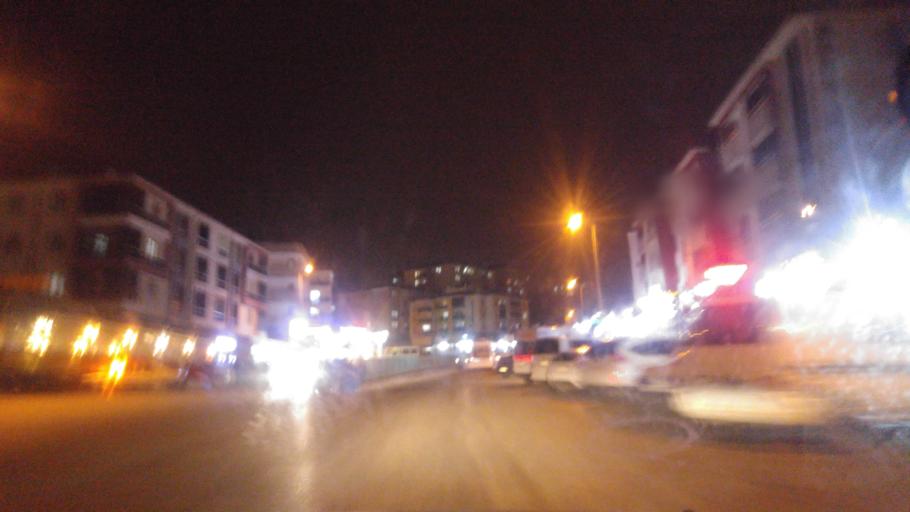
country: TR
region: Karabuk
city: Karabuk
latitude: 41.2197
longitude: 32.6603
